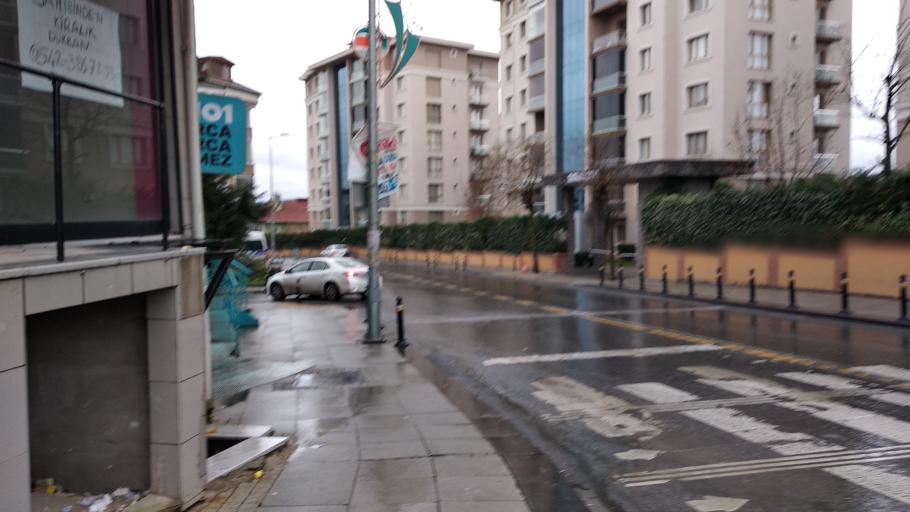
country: TR
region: Istanbul
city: Samandira
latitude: 41.0244
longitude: 29.1831
